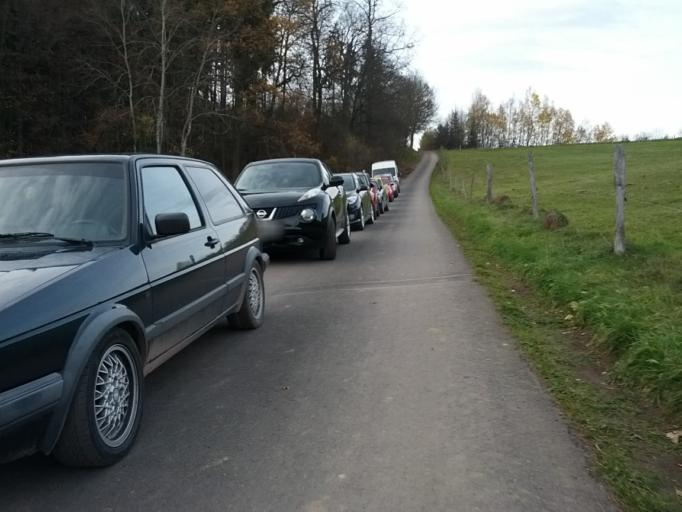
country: DE
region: Thuringia
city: Ruhla
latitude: 50.9353
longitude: 10.3436
